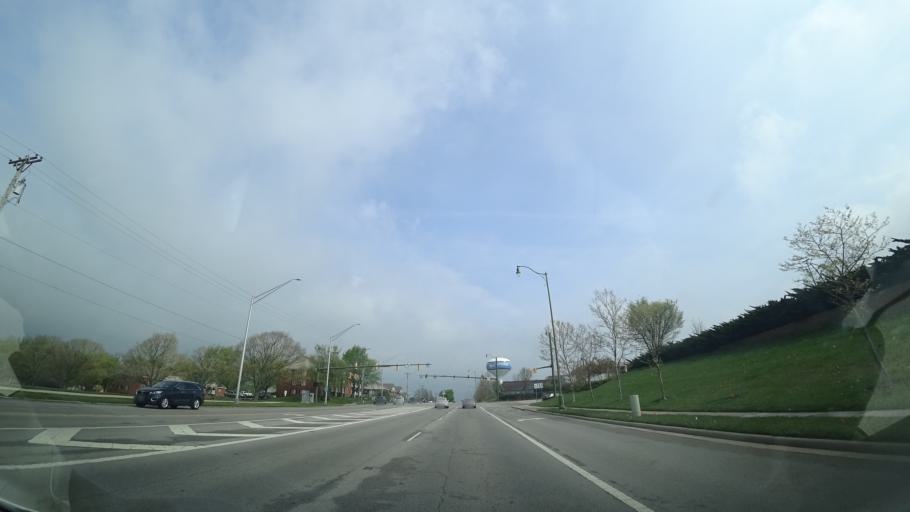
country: US
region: Ohio
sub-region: Greene County
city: Beavercreek
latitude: 39.6933
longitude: -84.1063
